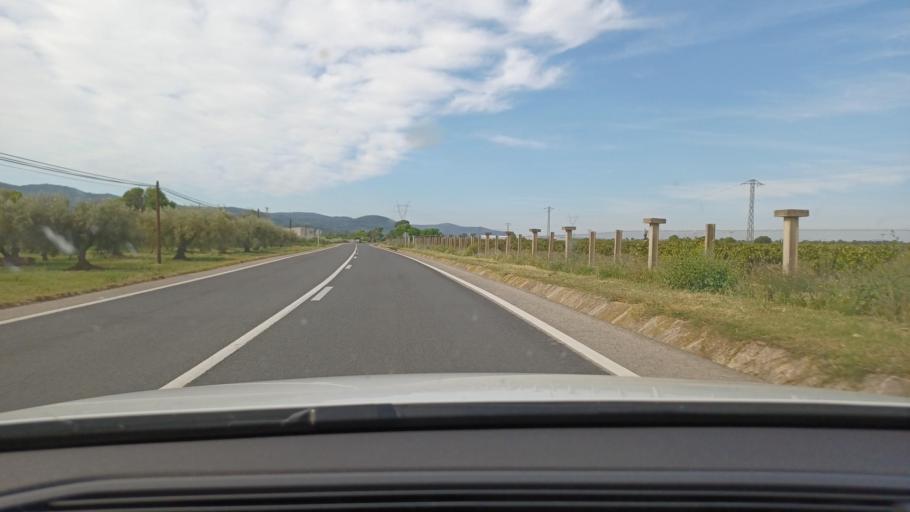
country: ES
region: Catalonia
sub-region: Provincia de Tarragona
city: Santa Barbara
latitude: 40.6979
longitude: 0.4767
